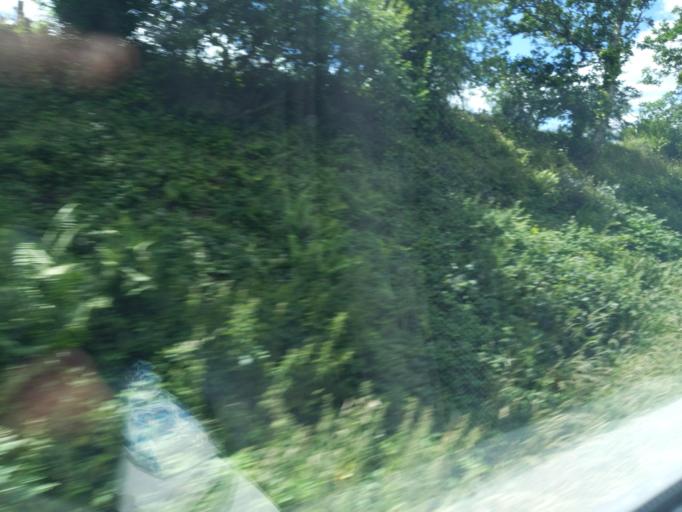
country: GB
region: England
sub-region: Cornwall
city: Liskeard
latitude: 50.4211
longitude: -4.3885
